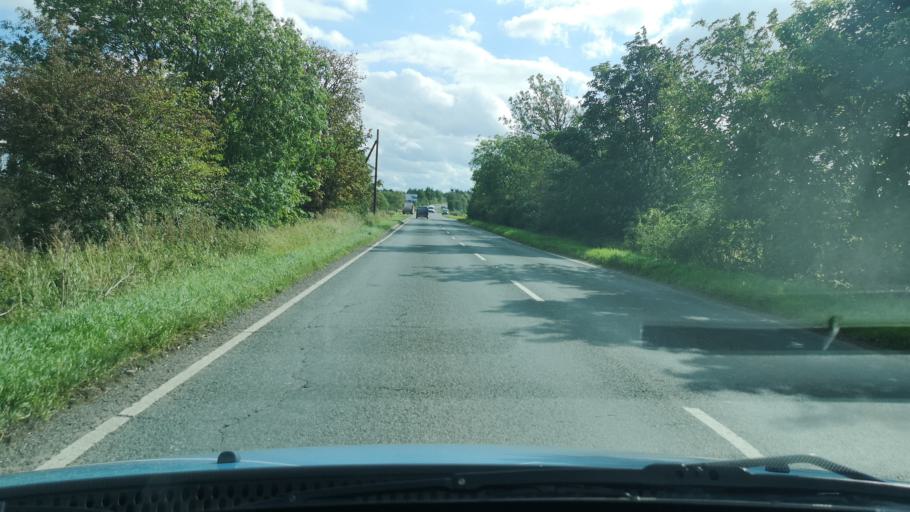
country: GB
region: England
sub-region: North Lincolnshire
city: Belton
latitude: 53.5746
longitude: -0.8176
